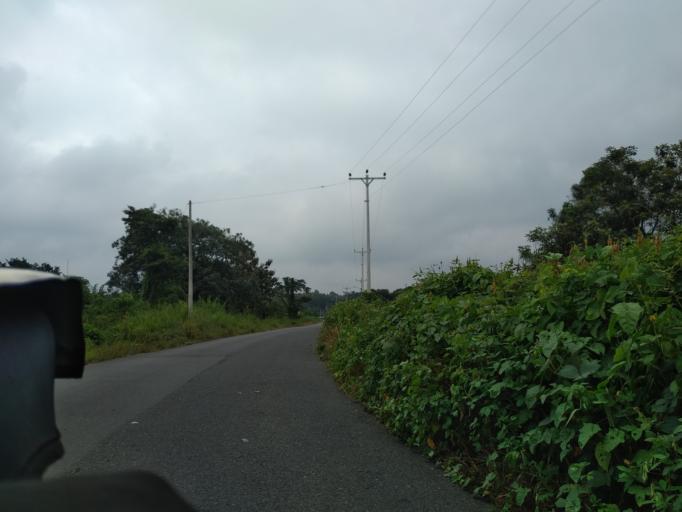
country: EC
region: Los Rios
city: Quevedo
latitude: -0.9766
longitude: -79.3534
